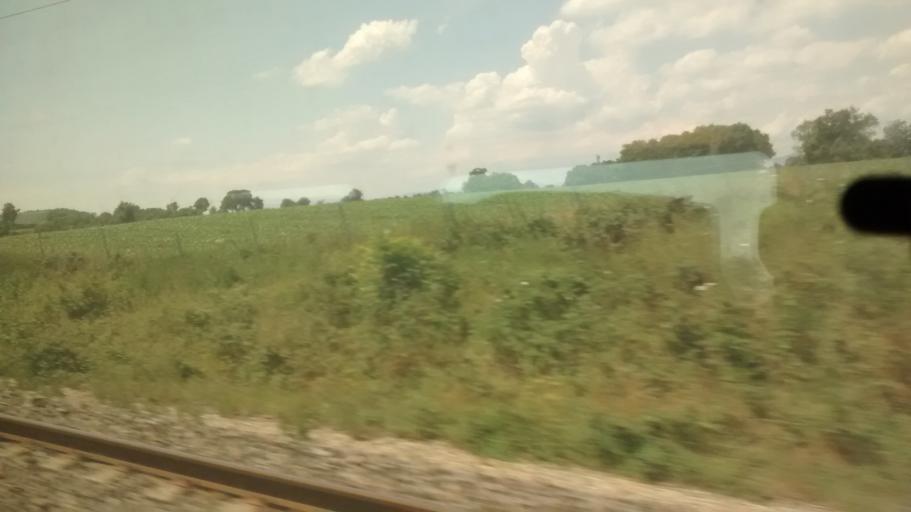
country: FR
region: Rhone-Alpes
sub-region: Departement de l'Ain
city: Grieges
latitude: 46.2235
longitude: 4.8579
